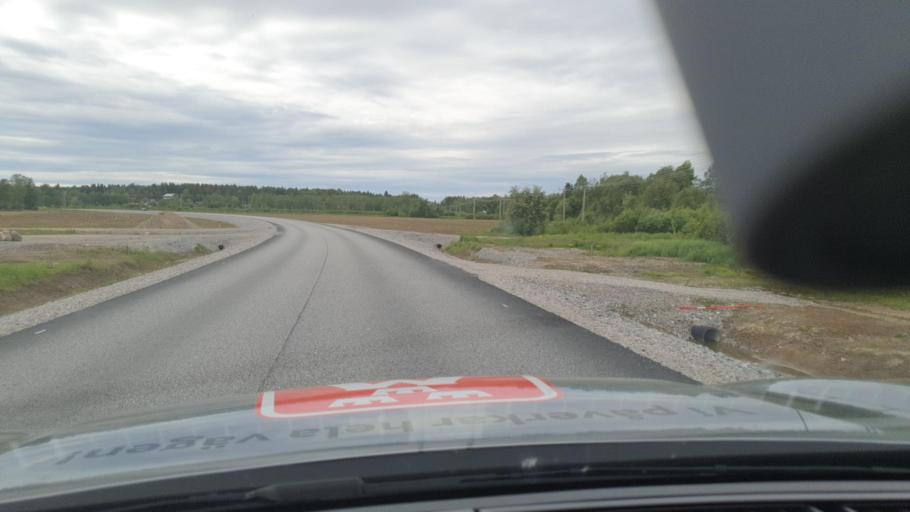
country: SE
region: Norrbotten
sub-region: Kalix Kommun
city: Rolfs
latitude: 65.8830
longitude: 23.0626
